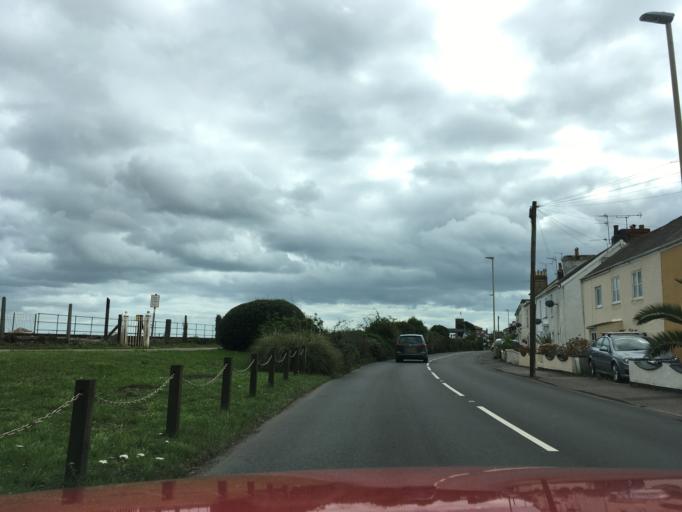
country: GB
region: England
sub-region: Devon
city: Starcross
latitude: 50.6299
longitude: -3.4490
